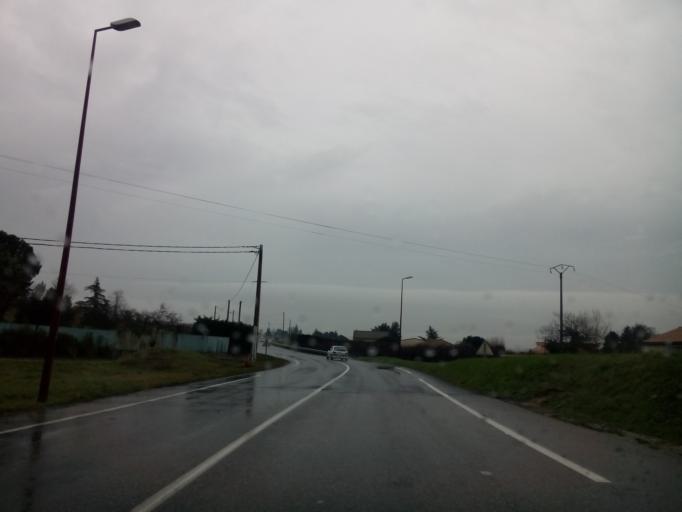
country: FR
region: Rhone-Alpes
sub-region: Departement de la Drome
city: Mercurol
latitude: 45.0684
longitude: 4.8753
